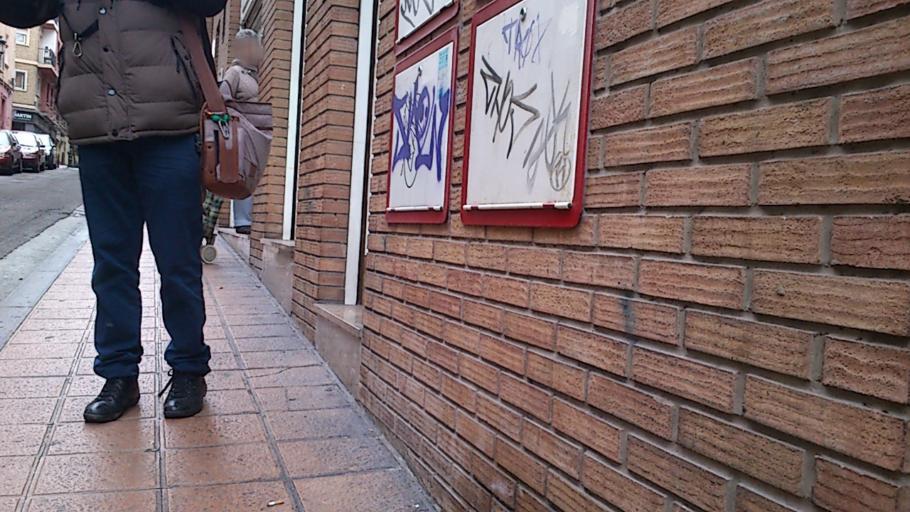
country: ES
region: Aragon
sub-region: Provincia de Zaragoza
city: Zaragoza
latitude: 41.6498
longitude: -0.8706
